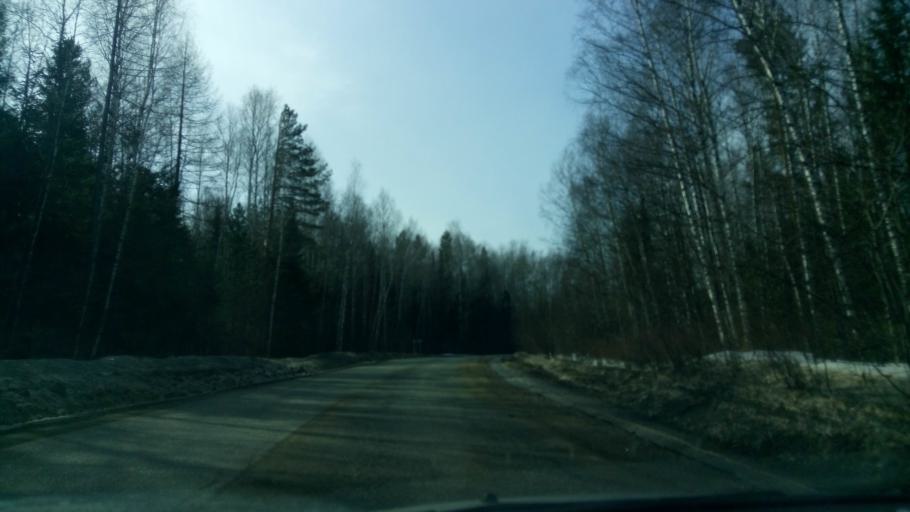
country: RU
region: Sverdlovsk
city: Uralets
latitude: 57.6974
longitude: 59.7608
